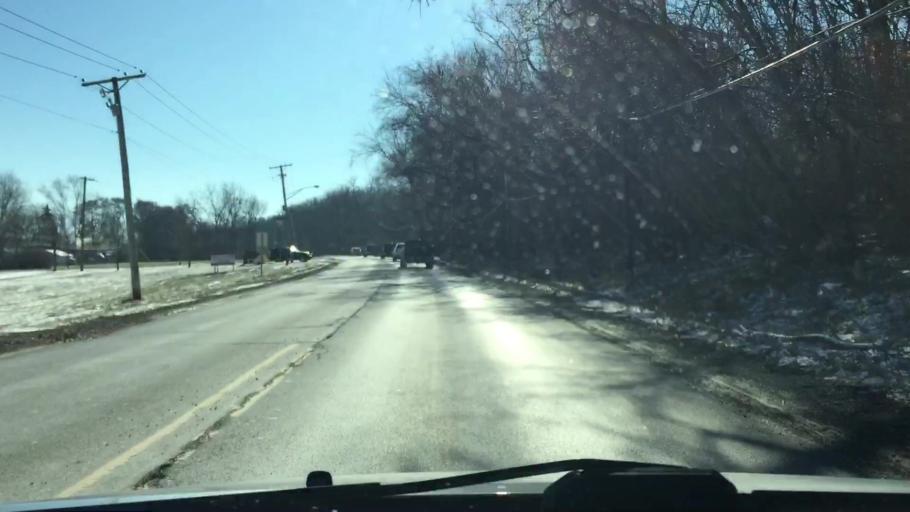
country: US
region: Illinois
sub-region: Kane County
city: Sleepy Hollow
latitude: 42.1219
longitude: -88.3000
